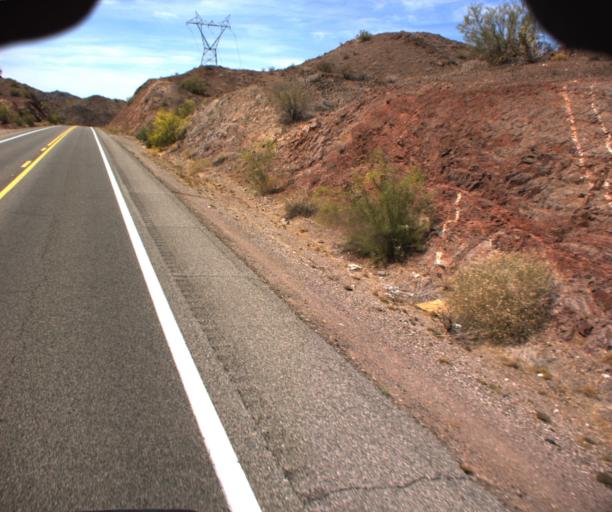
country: US
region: Arizona
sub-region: La Paz County
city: Cienega Springs
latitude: 34.3483
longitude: -114.1516
